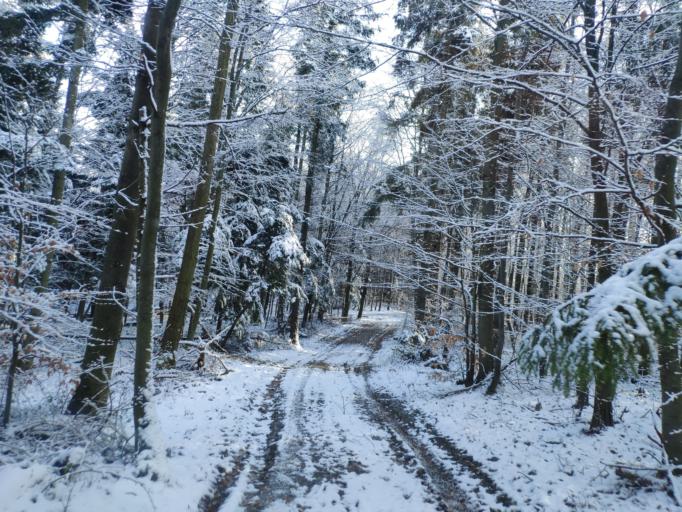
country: SK
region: Kosicky
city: Moldava nad Bodvou
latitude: 48.7439
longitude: 21.0876
